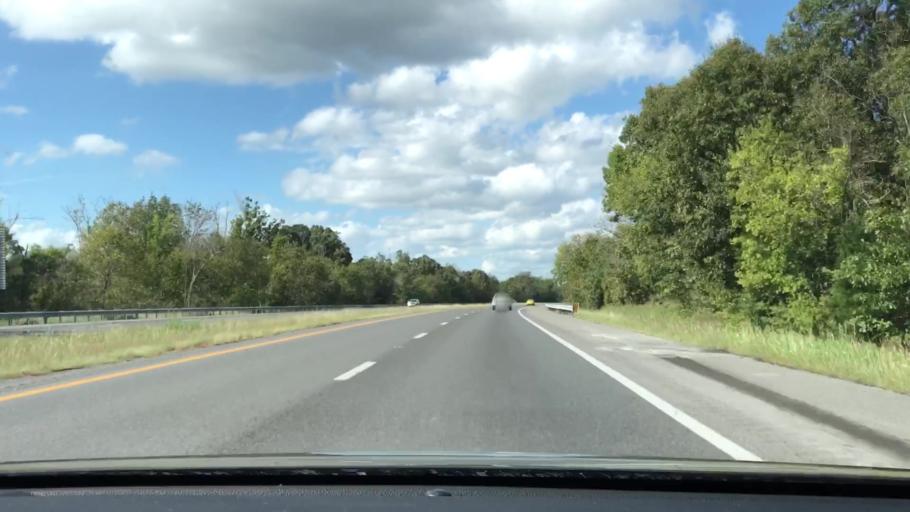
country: US
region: Kentucky
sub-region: Marshall County
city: Benton
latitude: 36.9450
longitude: -88.3482
